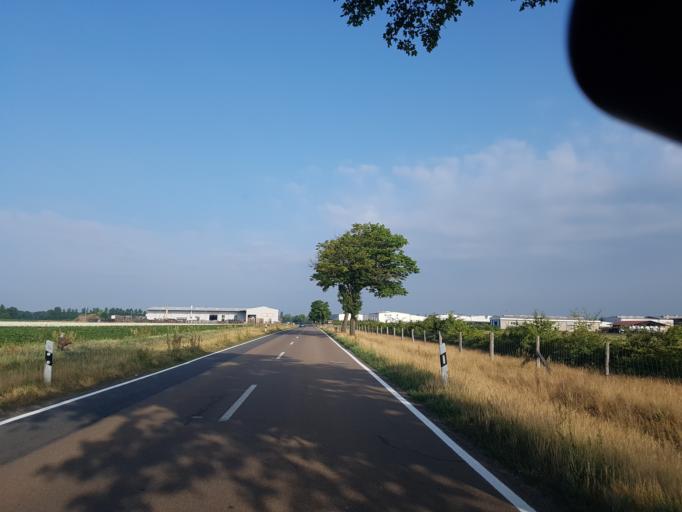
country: DE
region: Saxony-Anhalt
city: Holzdorf
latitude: 51.8525
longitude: 13.1146
